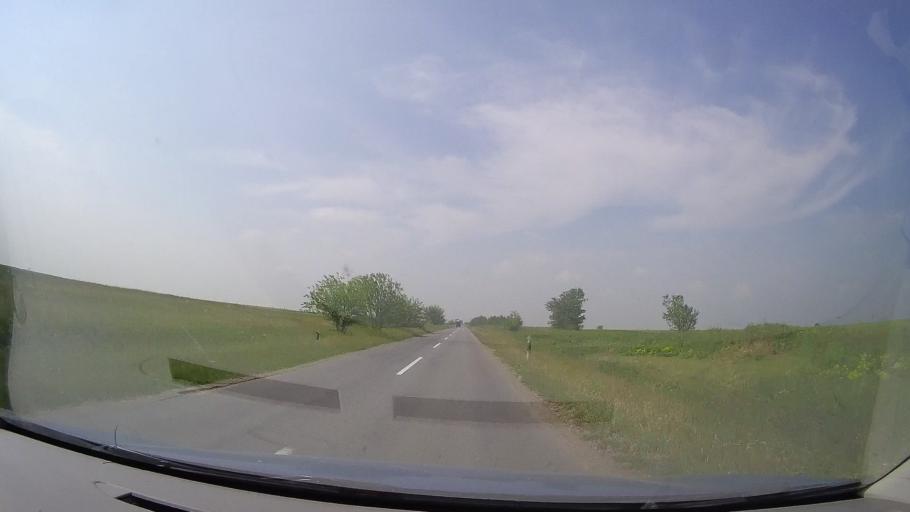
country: RS
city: Padina
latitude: 45.1583
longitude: 20.7488
